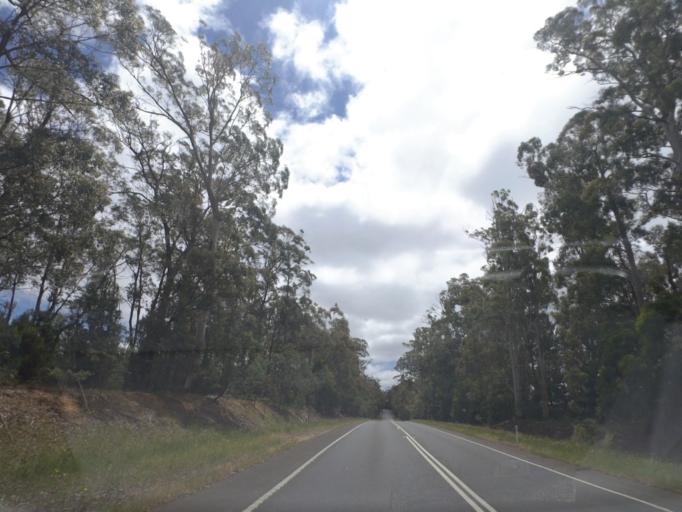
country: AU
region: Victoria
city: Brown Hill
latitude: -37.4899
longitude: 144.1540
